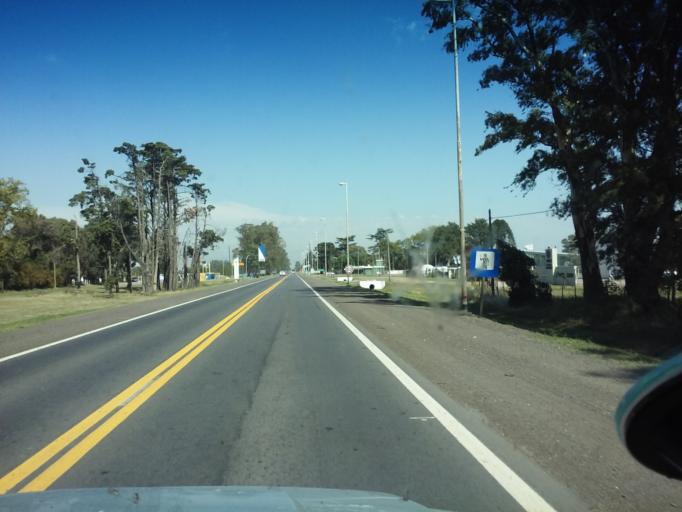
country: AR
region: Buenos Aires
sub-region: Partido de Nueve de Julio
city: Nueve de Julio
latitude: -35.4789
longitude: -60.8707
